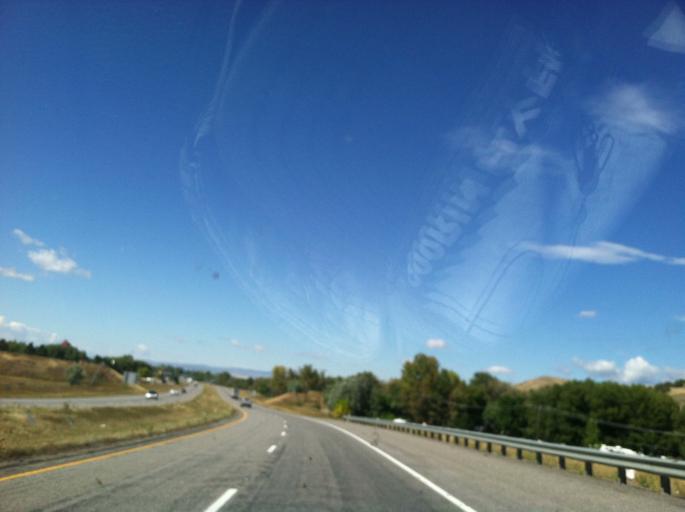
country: US
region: Montana
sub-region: Gallatin County
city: Bozeman
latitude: 45.6827
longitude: -111.0131
